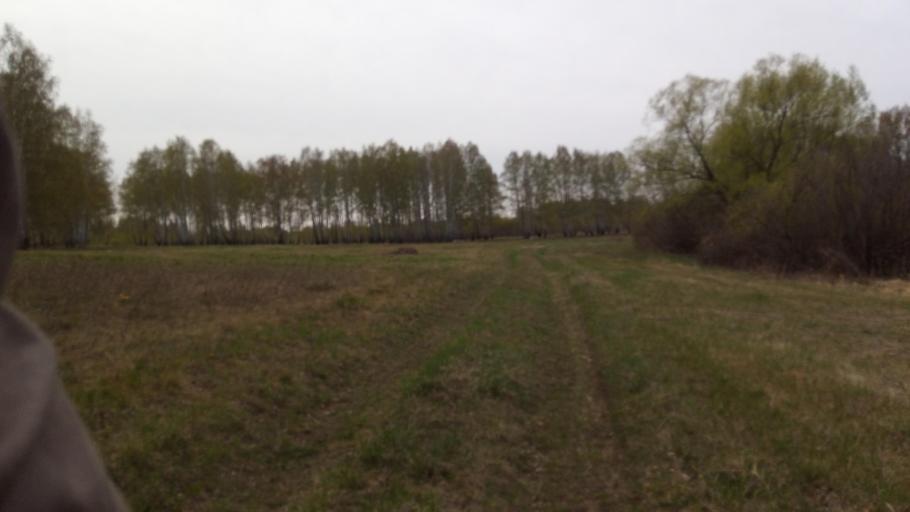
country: RU
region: Chelyabinsk
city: Timiryazevskiy
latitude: 54.9999
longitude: 60.8515
